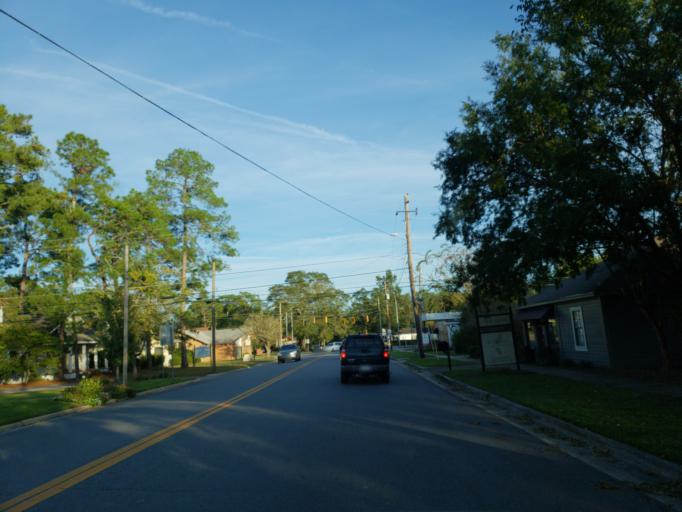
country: US
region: Georgia
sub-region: Tift County
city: Tifton
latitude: 31.4635
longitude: -83.5067
